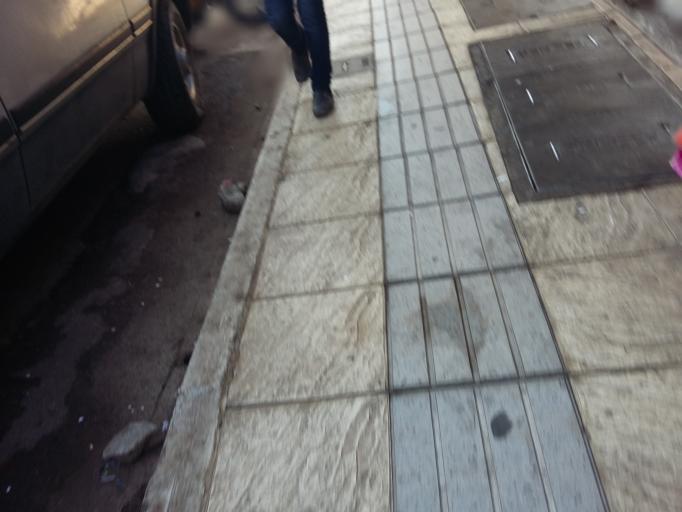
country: MX
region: Guerrero
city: Chilpancingo de los Bravos
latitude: 17.5509
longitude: -99.5008
